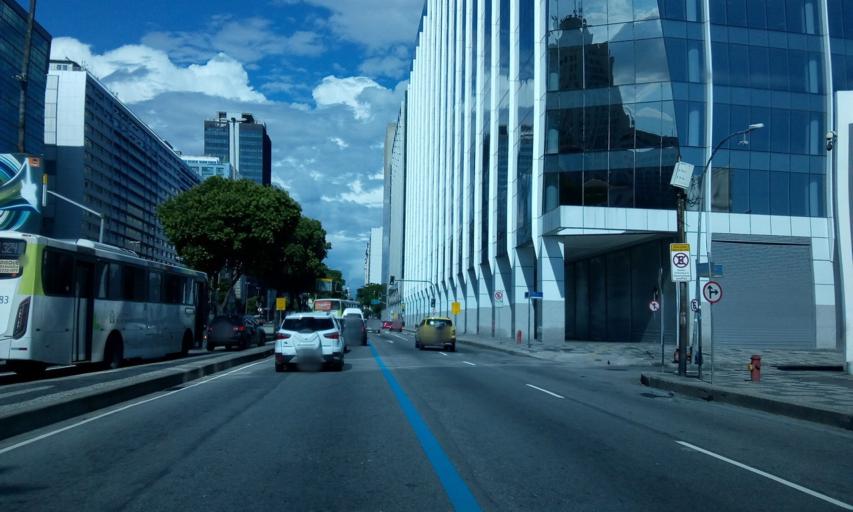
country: BR
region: Rio de Janeiro
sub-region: Rio De Janeiro
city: Rio de Janeiro
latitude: -22.9042
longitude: -43.1871
